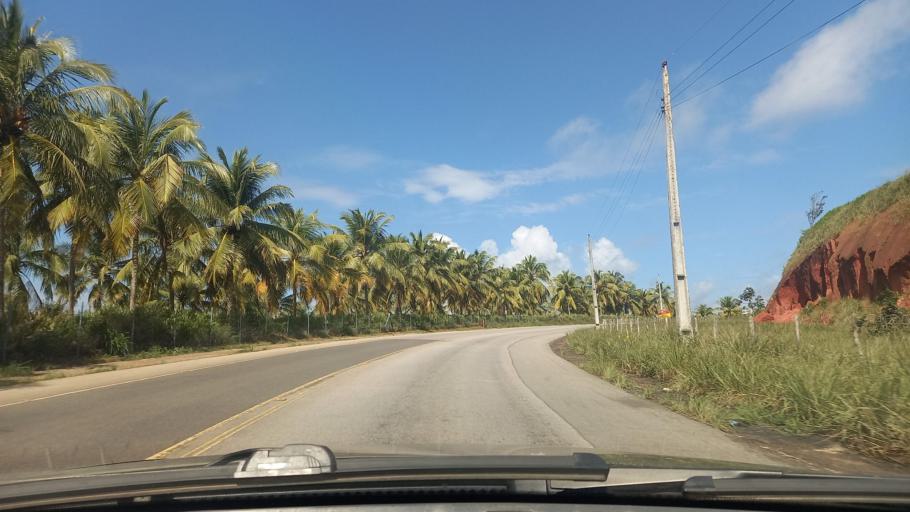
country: BR
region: Alagoas
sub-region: Marechal Deodoro
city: Marechal Deodoro
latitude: -9.8622
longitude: -35.9161
